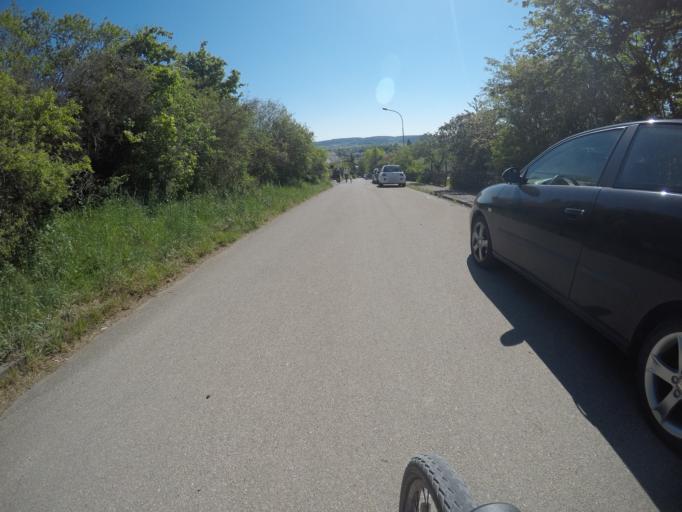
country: DE
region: Baden-Wuerttemberg
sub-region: Karlsruhe Region
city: Heimsheim
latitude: 48.8144
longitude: 8.8652
